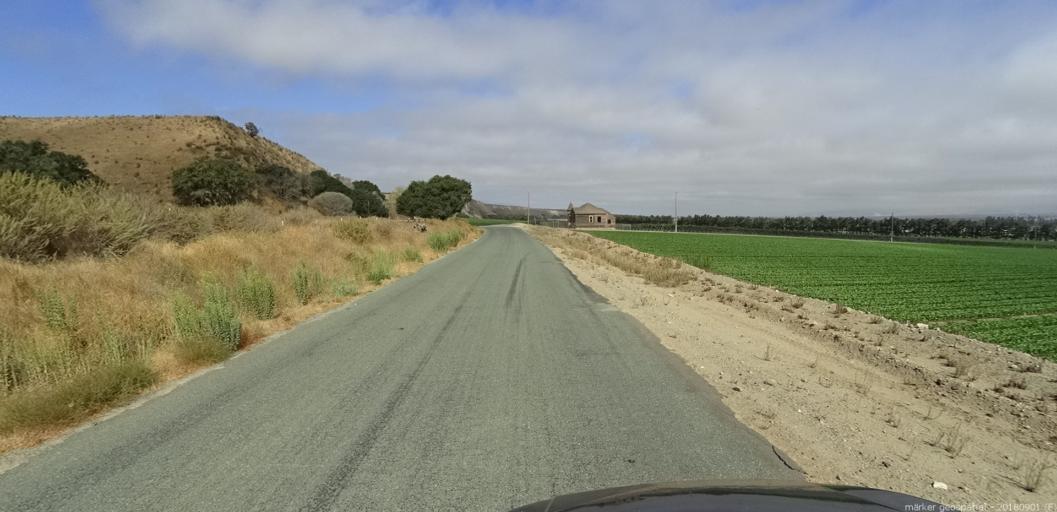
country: US
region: California
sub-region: Monterey County
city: Soledad
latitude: 36.4051
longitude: -121.3810
